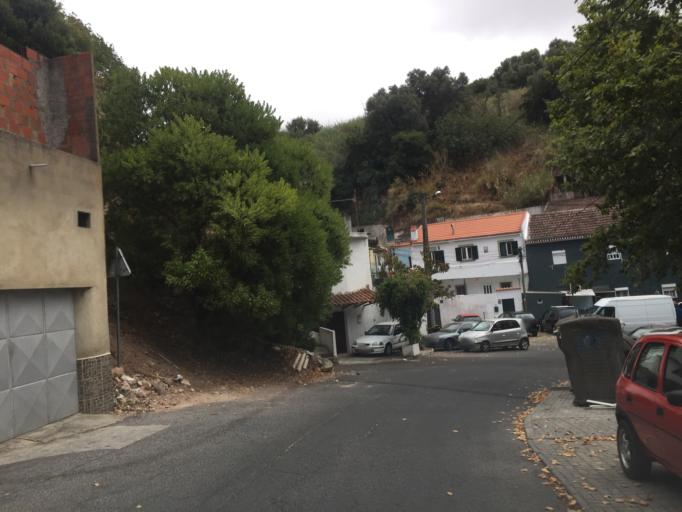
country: PT
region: Lisbon
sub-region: Odivelas
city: Olival do Basto
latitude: 38.7948
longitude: -9.1561
